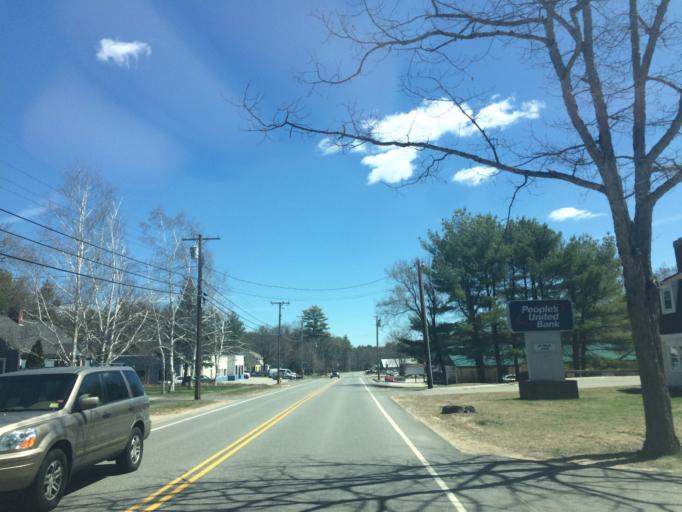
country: US
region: Maine
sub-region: Oxford County
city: Porter
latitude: 43.8063
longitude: -70.8767
